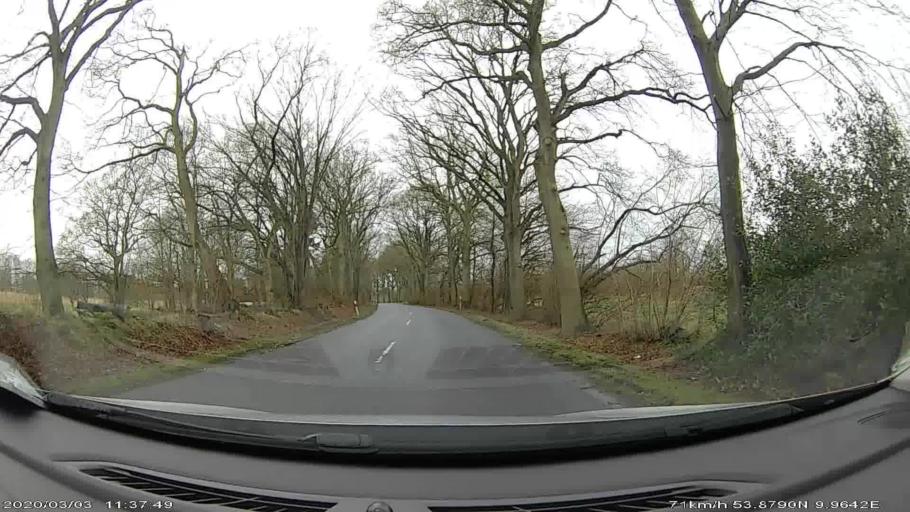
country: DE
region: Schleswig-Holstein
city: Schmalfeld
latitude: 53.8796
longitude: 9.9600
